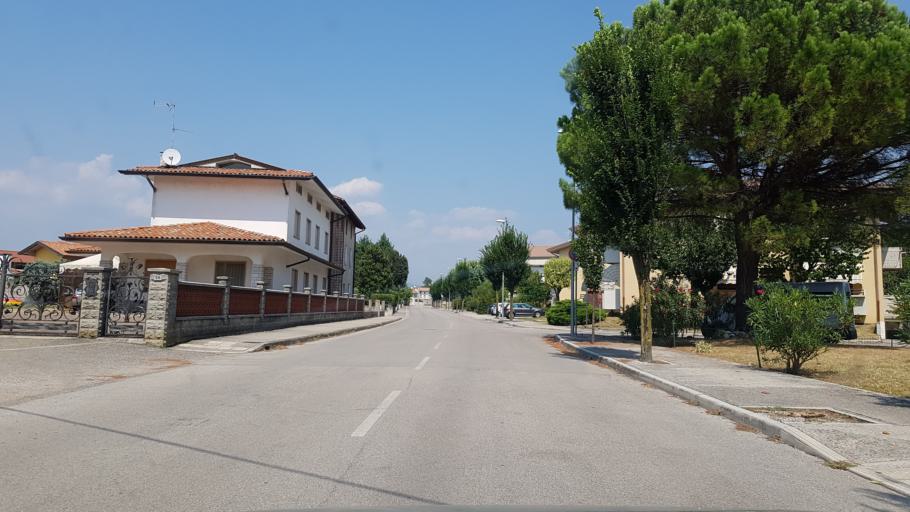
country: IT
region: Friuli Venezia Giulia
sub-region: Provincia di Gorizia
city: Farra d'Isonzo
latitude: 45.9081
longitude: 13.5140
